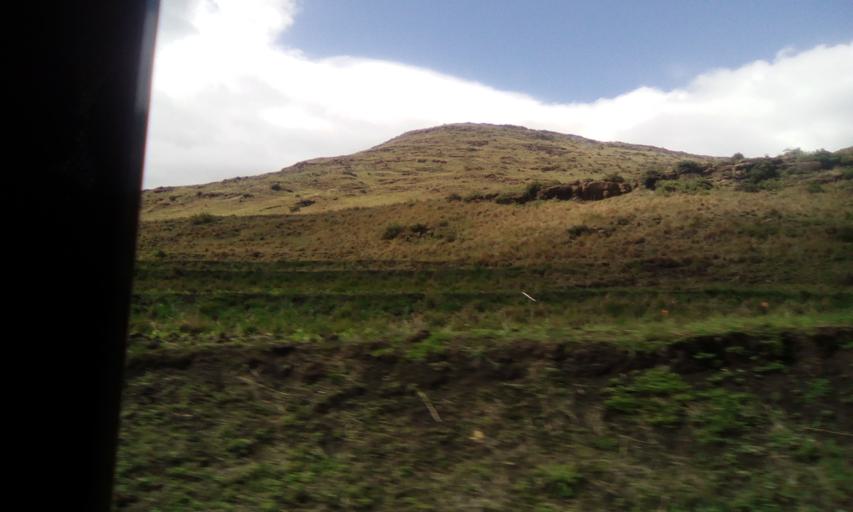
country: LS
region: Maseru
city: Nako
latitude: -29.6564
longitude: 27.8526
